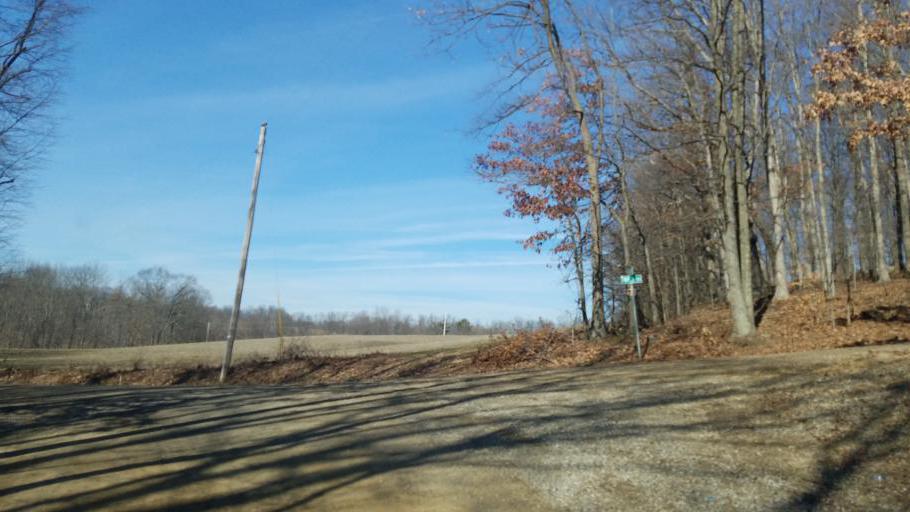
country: US
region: Ohio
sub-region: Ashland County
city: Loudonville
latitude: 40.5652
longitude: -82.3268
